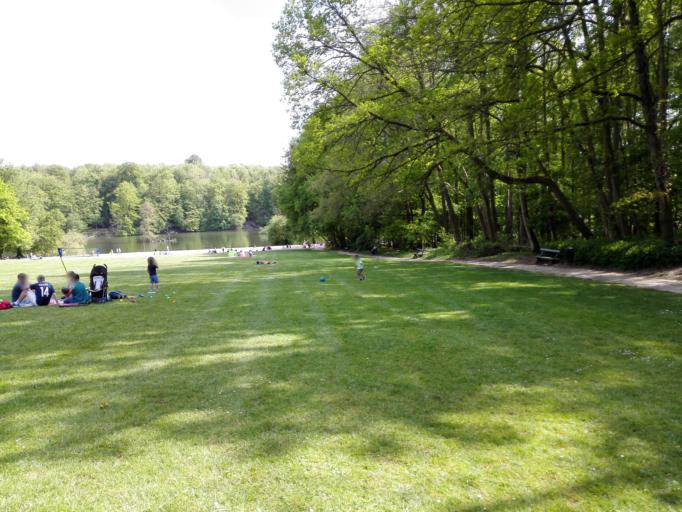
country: BE
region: Flanders
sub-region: Provincie Vlaams-Brabant
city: Tervuren
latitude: 50.8268
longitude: 4.5166
